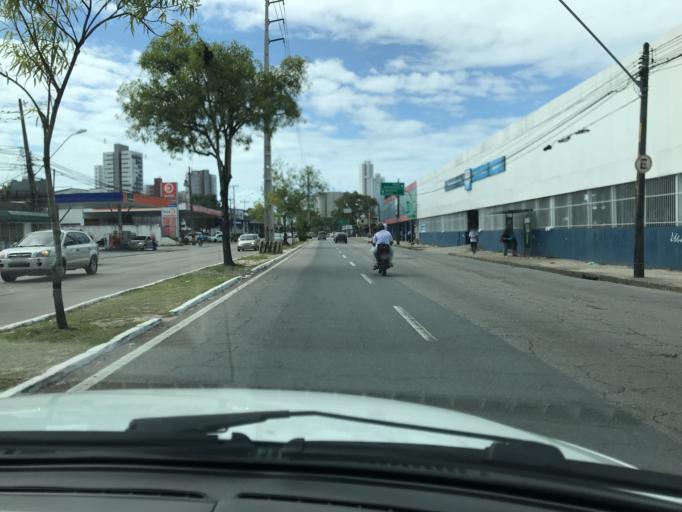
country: BR
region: Pernambuco
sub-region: Recife
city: Recife
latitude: -8.0625
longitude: -34.9147
